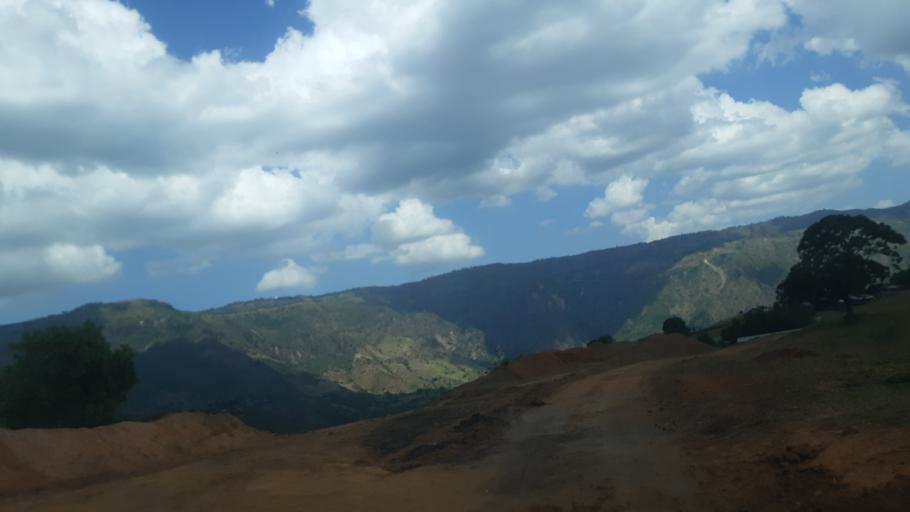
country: ET
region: Amhara
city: Dabat
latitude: 13.3368
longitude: 37.4204
